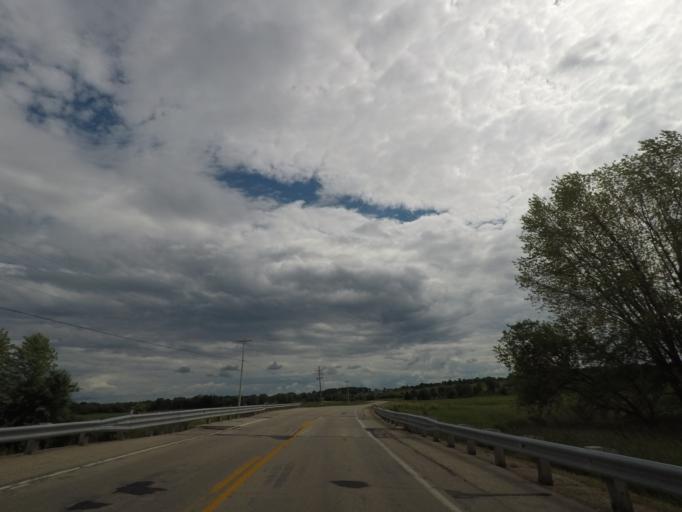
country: US
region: Wisconsin
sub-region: Dane County
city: Belleville
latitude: 42.8489
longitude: -89.5243
